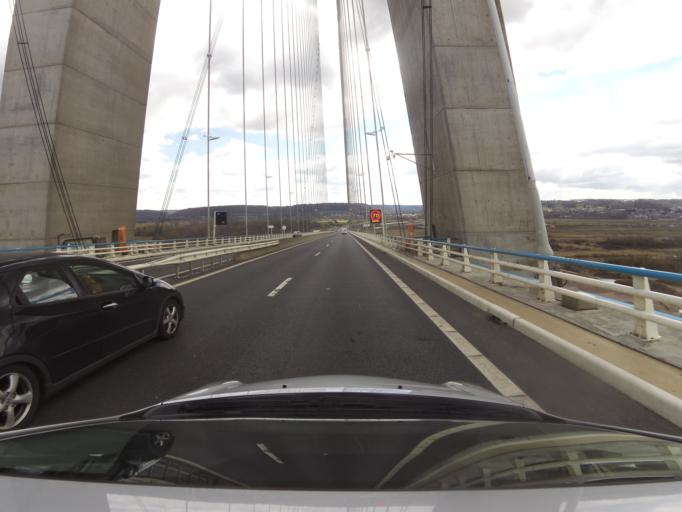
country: FR
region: Lower Normandy
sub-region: Departement du Calvados
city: La Riviere-Saint-Sauveur
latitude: 49.4288
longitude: 0.2744
